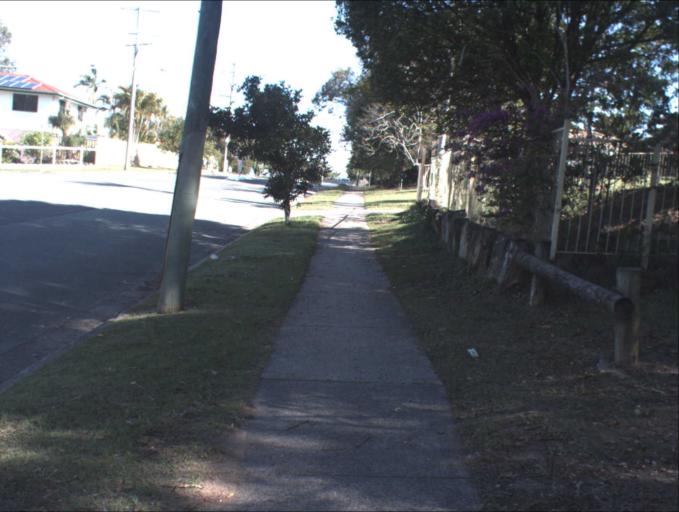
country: AU
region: Queensland
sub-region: Logan
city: Park Ridge South
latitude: -27.6804
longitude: 153.0273
